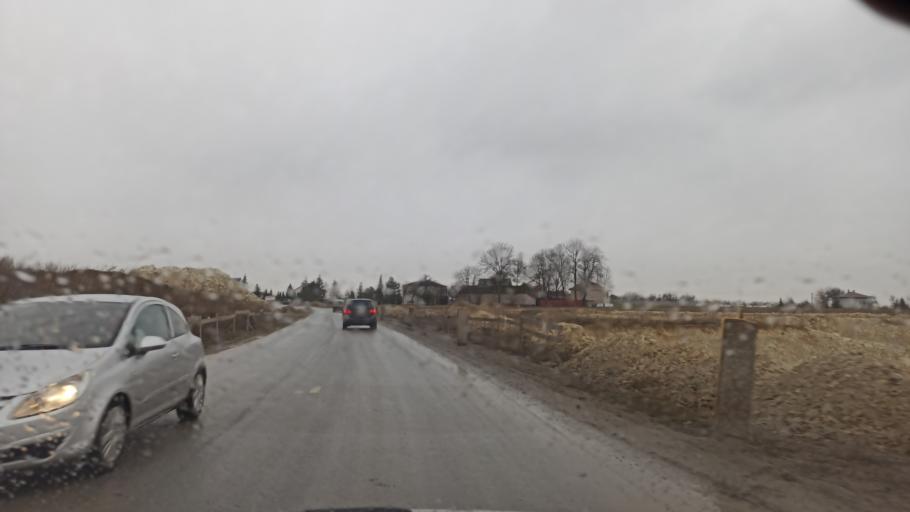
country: PL
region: Lublin Voivodeship
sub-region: Powiat lubelski
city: Niedrzwica Duza
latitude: 51.1031
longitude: 22.4071
